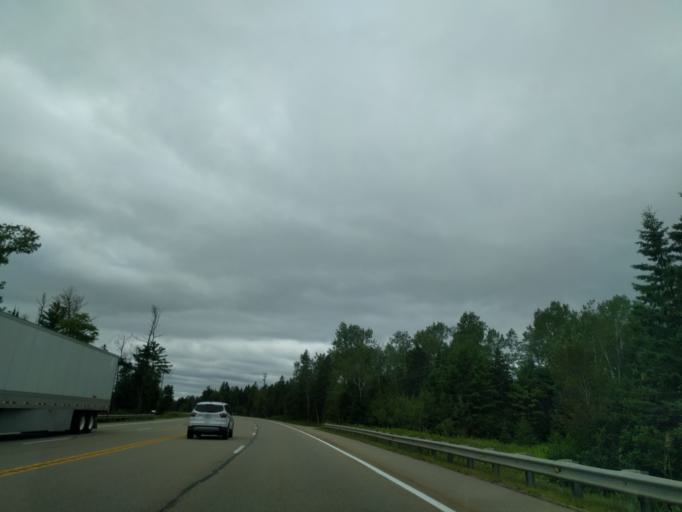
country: US
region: Michigan
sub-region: Delta County
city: Escanaba
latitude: 45.5409
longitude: -87.2783
